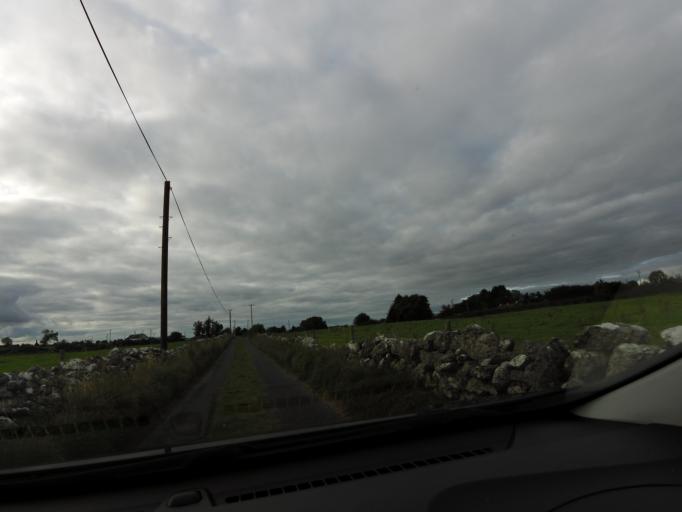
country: IE
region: Connaught
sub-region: County Galway
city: Ballinasloe
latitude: 53.3591
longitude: -8.0954
